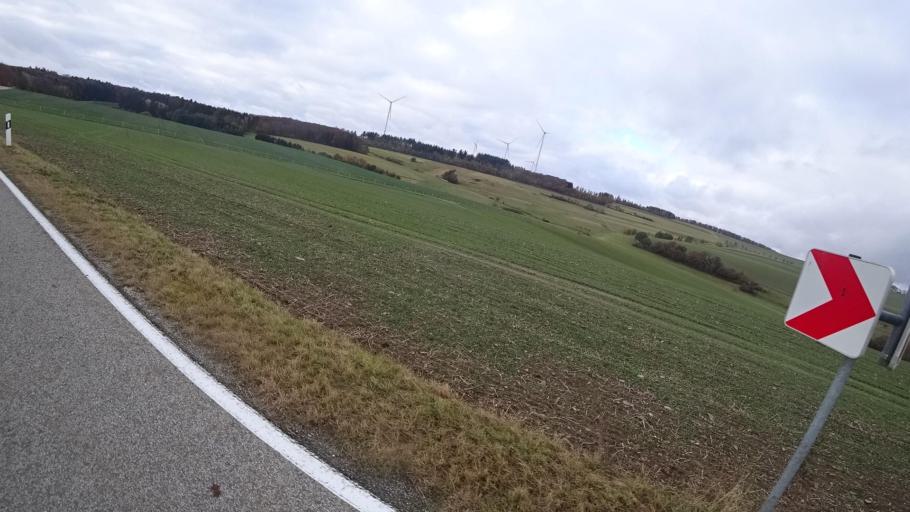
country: DE
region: Rheinland-Pfalz
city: Birkheim
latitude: 50.1170
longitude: 7.6179
